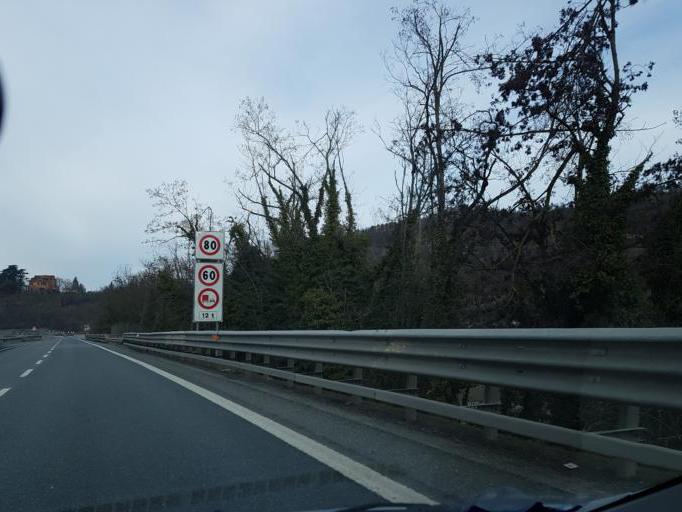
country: IT
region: Piedmont
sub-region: Provincia di Alessandria
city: Vignole Borbera
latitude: 44.7087
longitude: 8.8771
